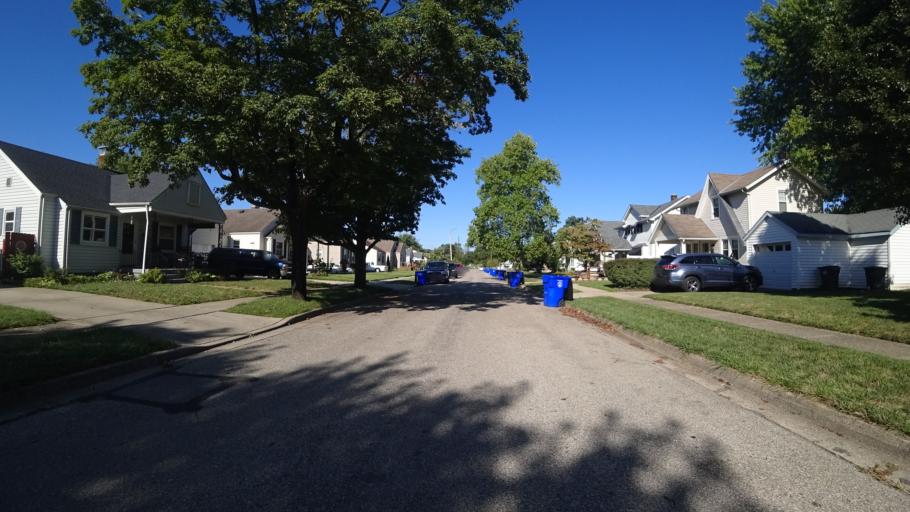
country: US
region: Ohio
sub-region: Butler County
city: Hamilton
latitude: 39.4064
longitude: -84.5354
